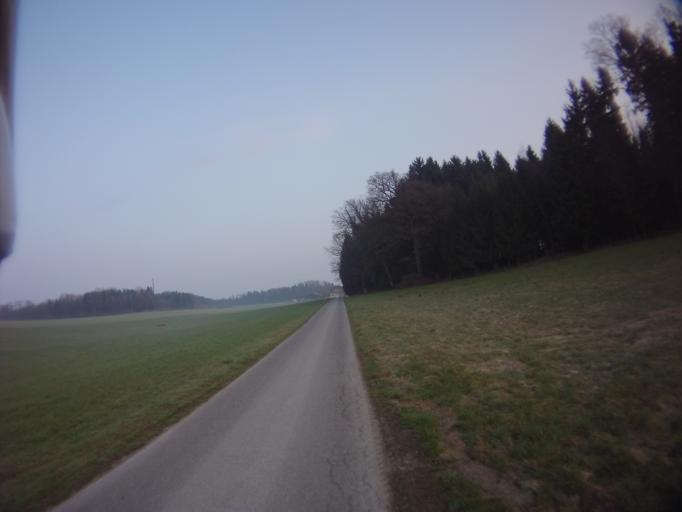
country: CH
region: Zug
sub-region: Zug
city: Cham
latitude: 47.2006
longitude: 8.4485
